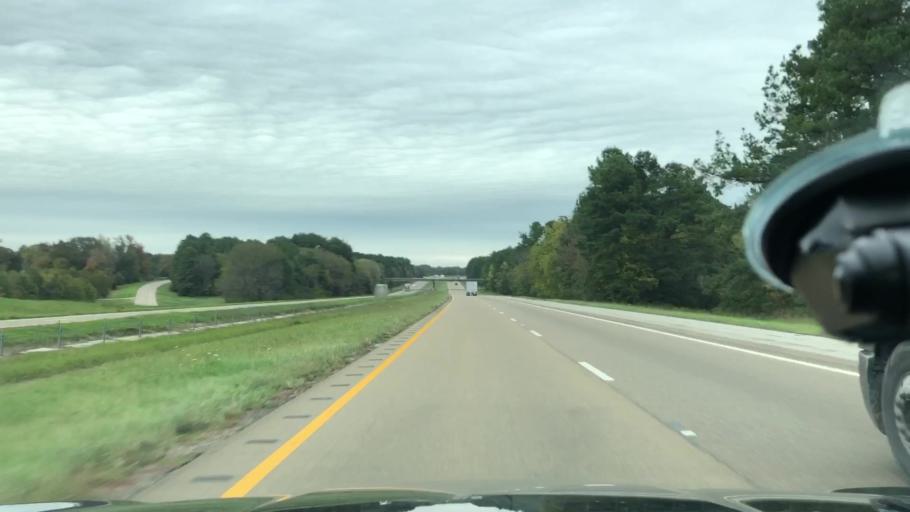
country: US
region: Texas
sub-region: Titus County
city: Mount Pleasant
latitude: 33.2194
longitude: -94.8940
